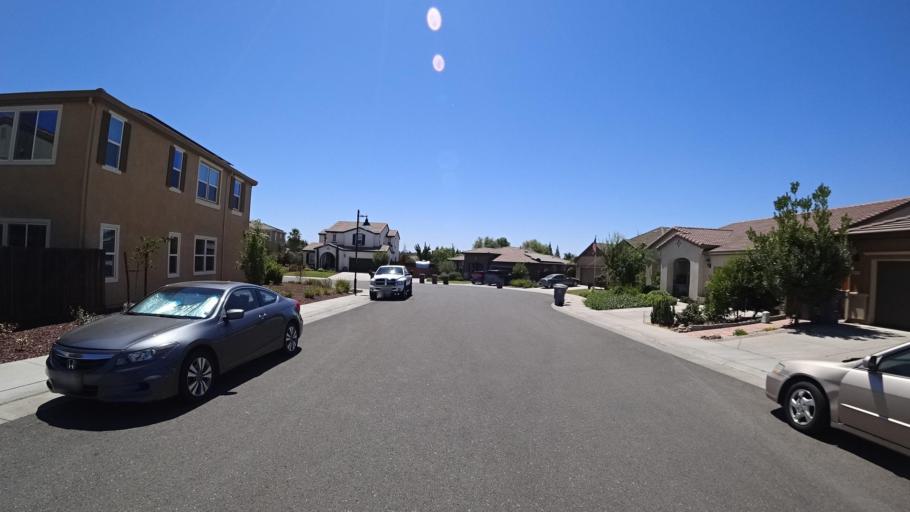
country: US
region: California
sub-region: Placer County
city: Rocklin
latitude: 38.8155
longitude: -121.2766
